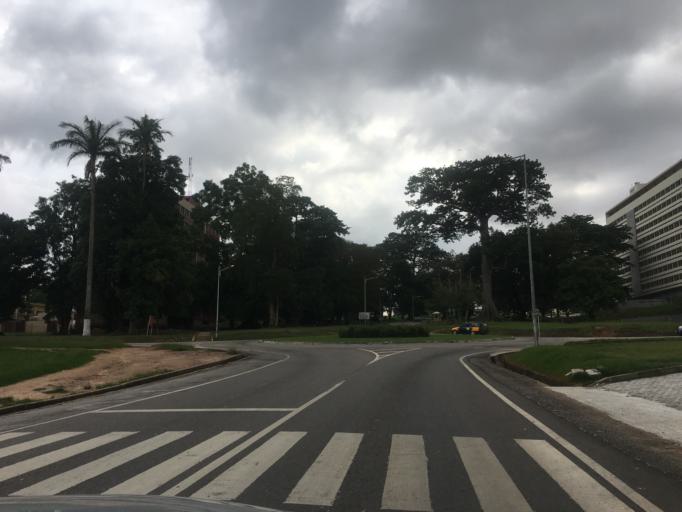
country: GH
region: Ashanti
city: Kumasi
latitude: 6.6787
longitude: -1.5704
